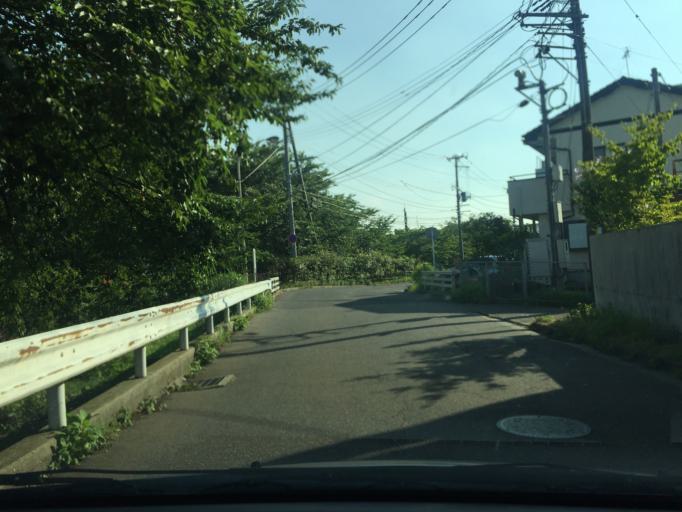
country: JP
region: Niigata
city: Niigata-shi
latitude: 37.8928
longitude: 139.0509
